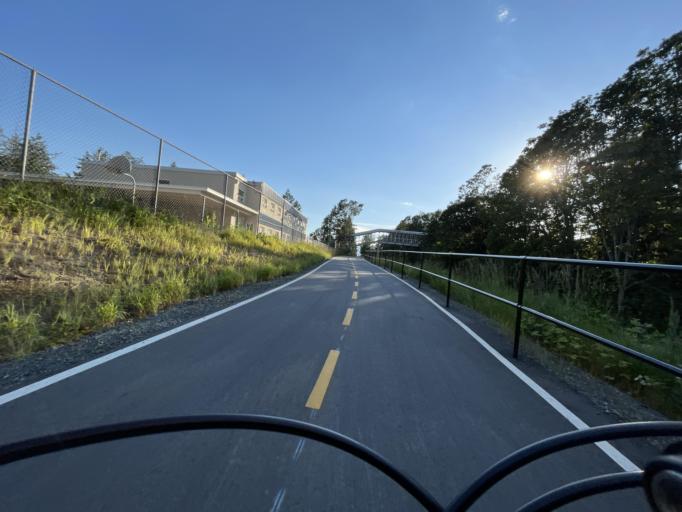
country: CA
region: British Columbia
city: Colwood
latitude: 48.4493
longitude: -123.4849
